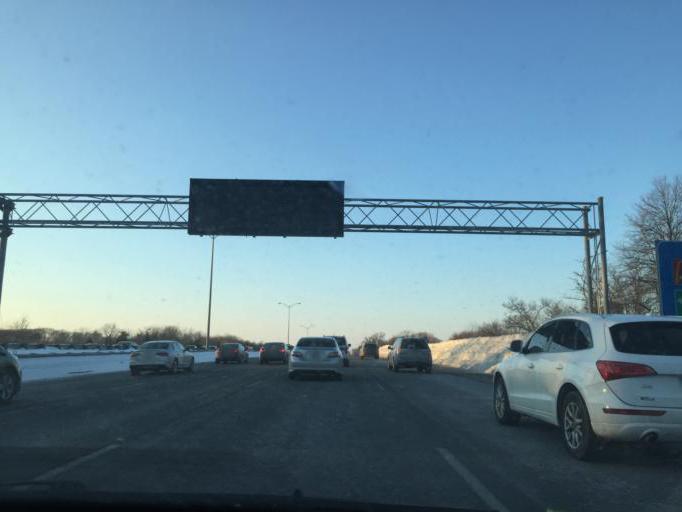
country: US
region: Massachusetts
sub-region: Middlesex County
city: Stoneham
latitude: 42.4681
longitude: -71.1063
